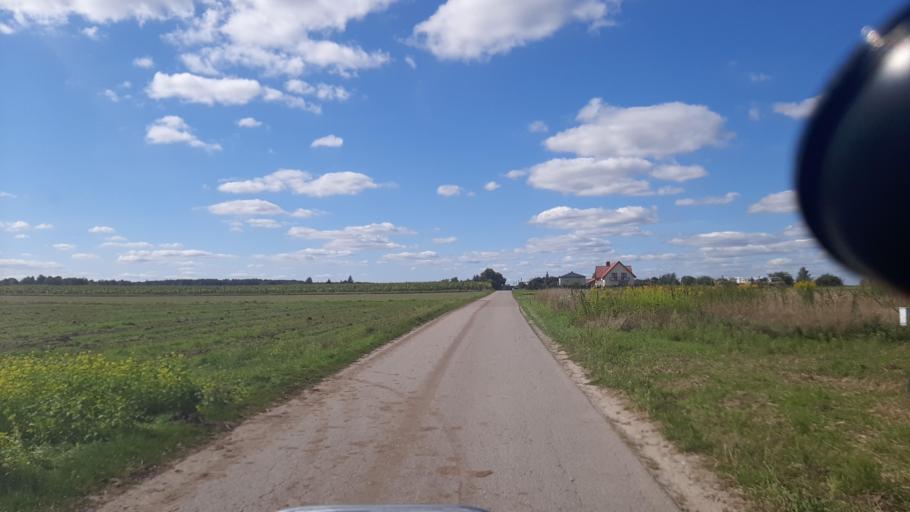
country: PL
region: Lublin Voivodeship
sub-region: Powiat lubartowski
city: Kamionka
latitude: 51.4051
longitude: 22.4068
